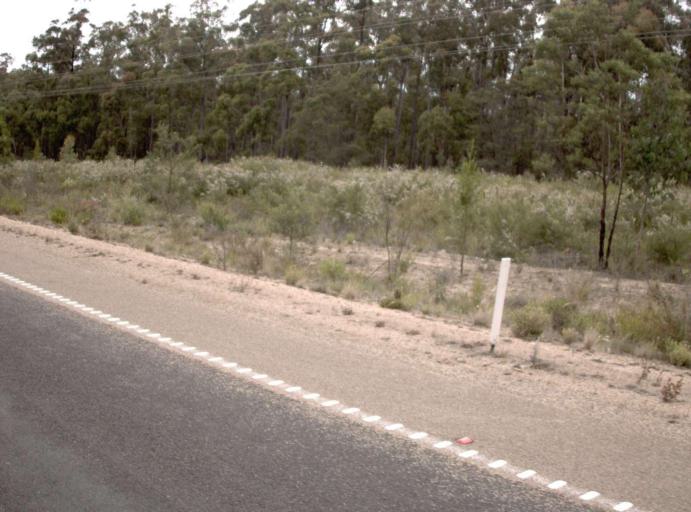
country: AU
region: Victoria
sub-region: East Gippsland
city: Lakes Entrance
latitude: -37.7003
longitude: 148.0500
